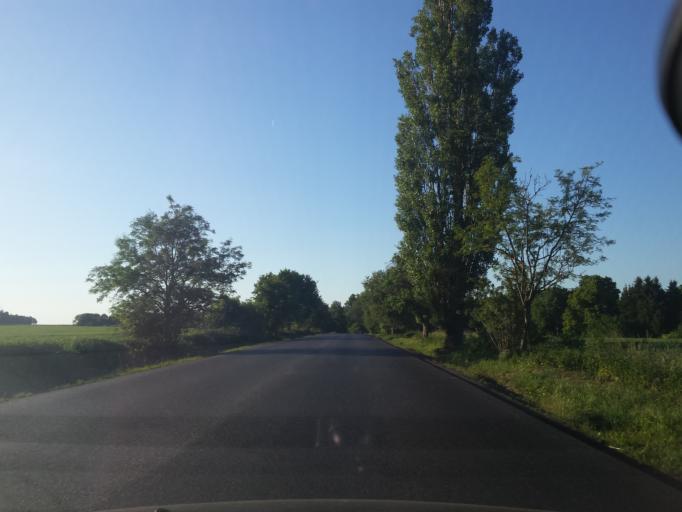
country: CZ
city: Duba
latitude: 50.5616
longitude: 14.5411
